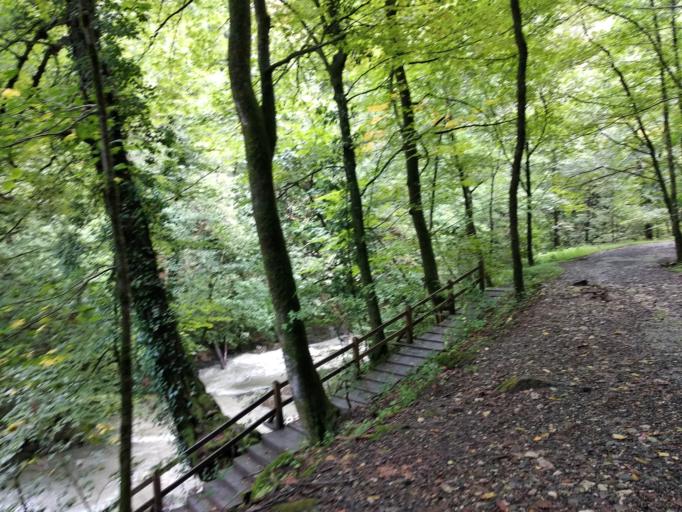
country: RU
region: Krasnodarskiy
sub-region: Sochi City
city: Sochi
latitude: 43.6381
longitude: 39.8116
